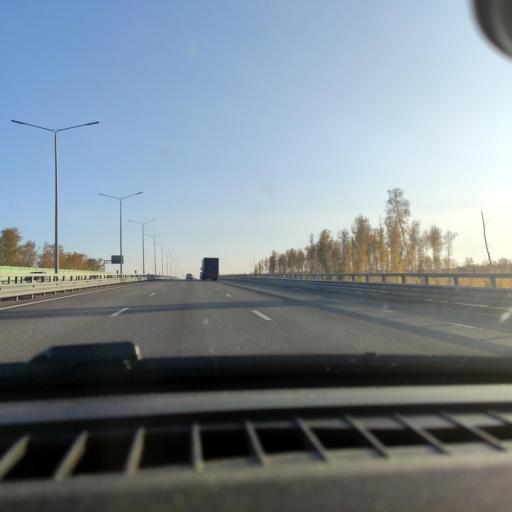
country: RU
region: Voronezj
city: Somovo
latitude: 51.7383
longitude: 39.3086
